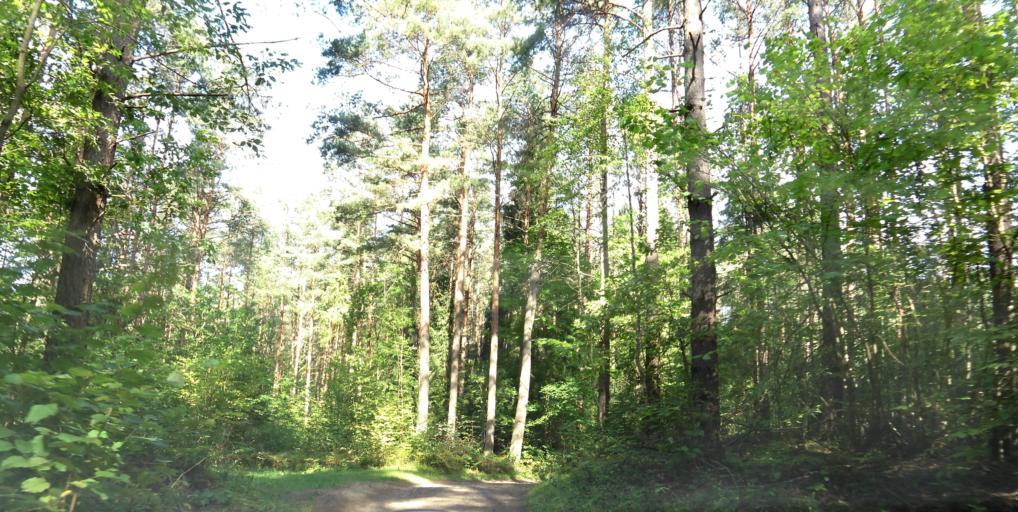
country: LT
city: Grigiskes
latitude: 54.7377
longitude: 25.0396
